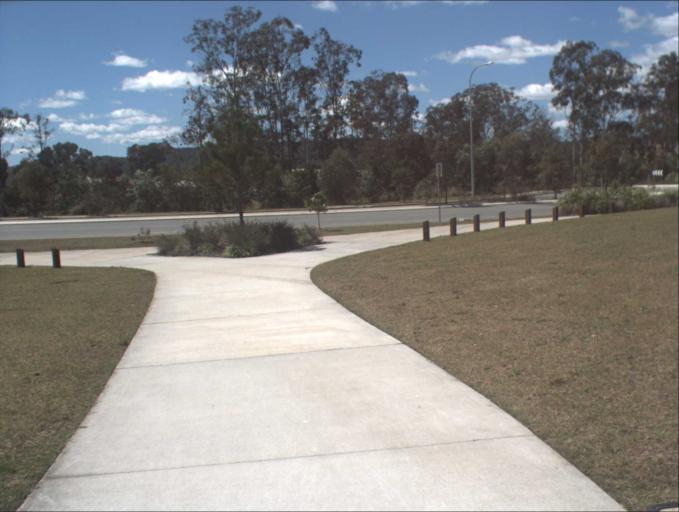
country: AU
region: Queensland
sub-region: Logan
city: Chambers Flat
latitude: -27.8034
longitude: 153.1087
